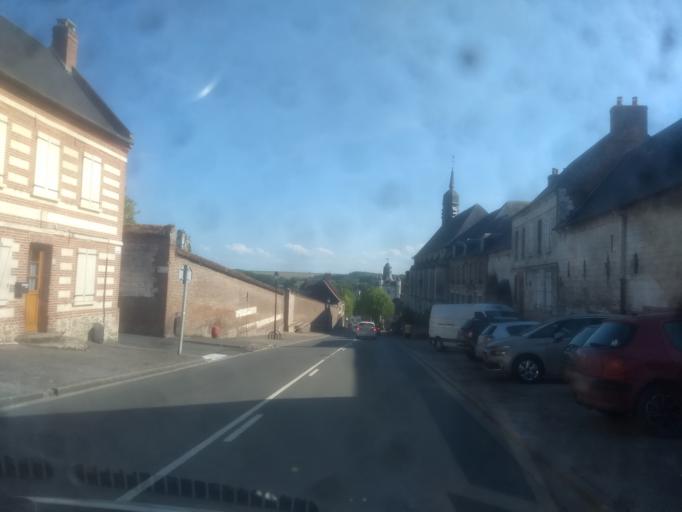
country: FR
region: Picardie
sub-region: Departement de la Somme
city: Saint-Riquier
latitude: 50.1362
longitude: 1.9460
